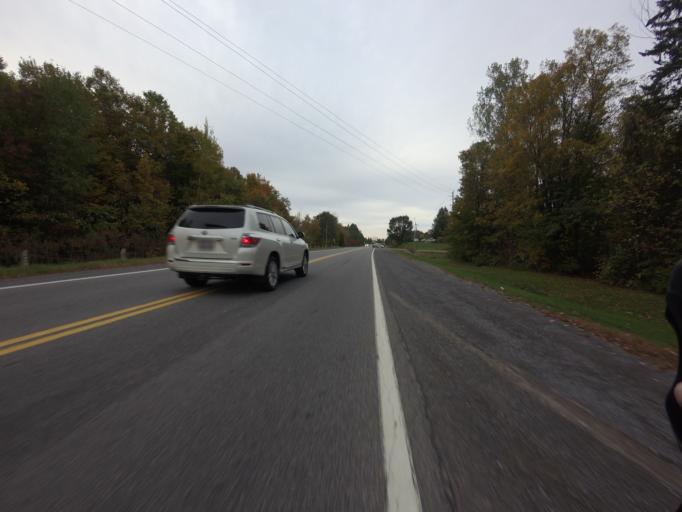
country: CA
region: Ontario
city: Bells Corners
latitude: 45.1528
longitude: -75.7102
